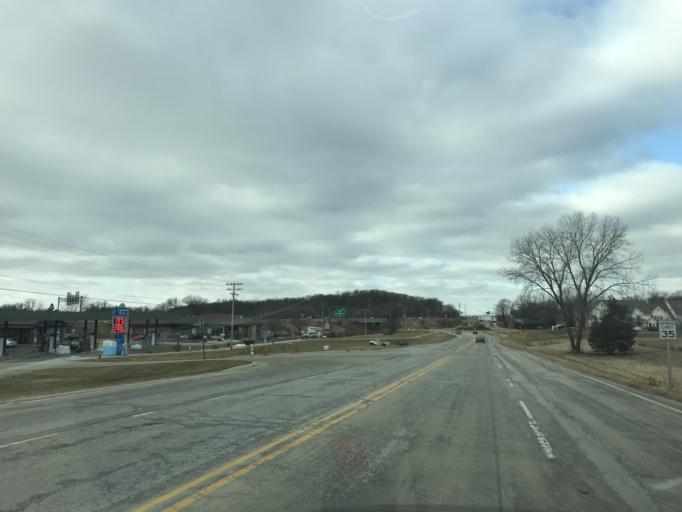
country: US
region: Wisconsin
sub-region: Dane County
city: Monona
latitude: 43.1065
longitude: -89.2966
